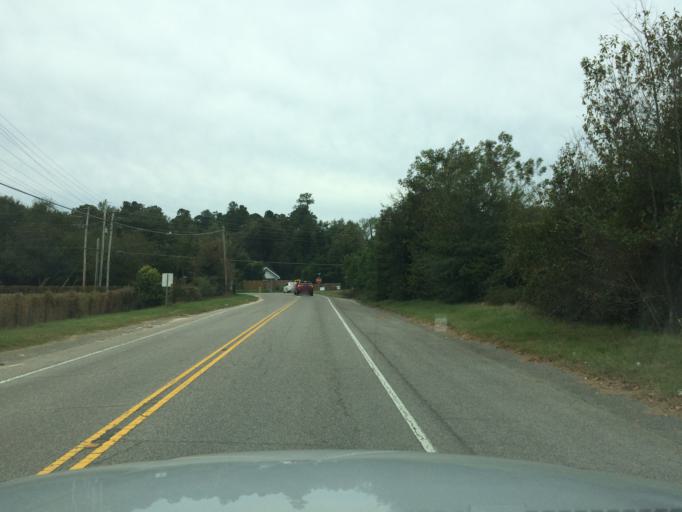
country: US
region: South Carolina
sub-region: Aiken County
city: New Ellenton
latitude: 33.3963
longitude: -81.7036
